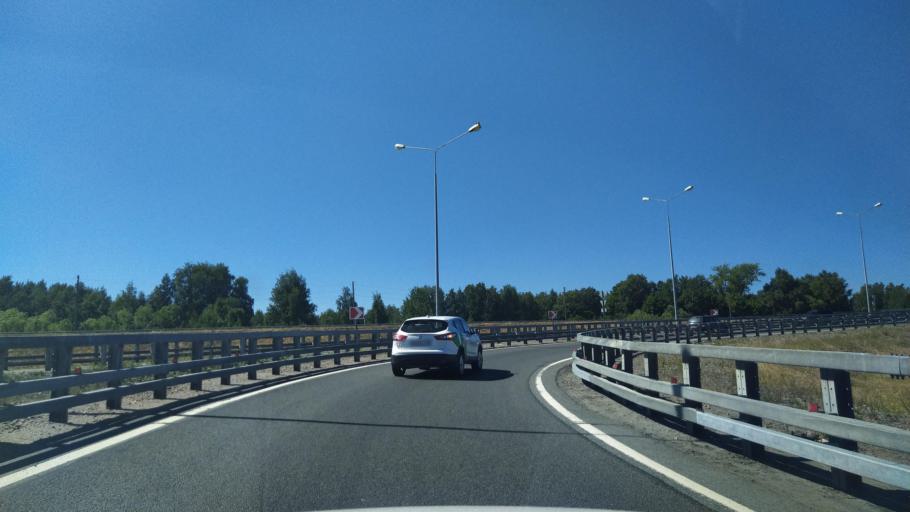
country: RU
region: St.-Petersburg
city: Kronshtadt
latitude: 60.0129
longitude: 29.7168
